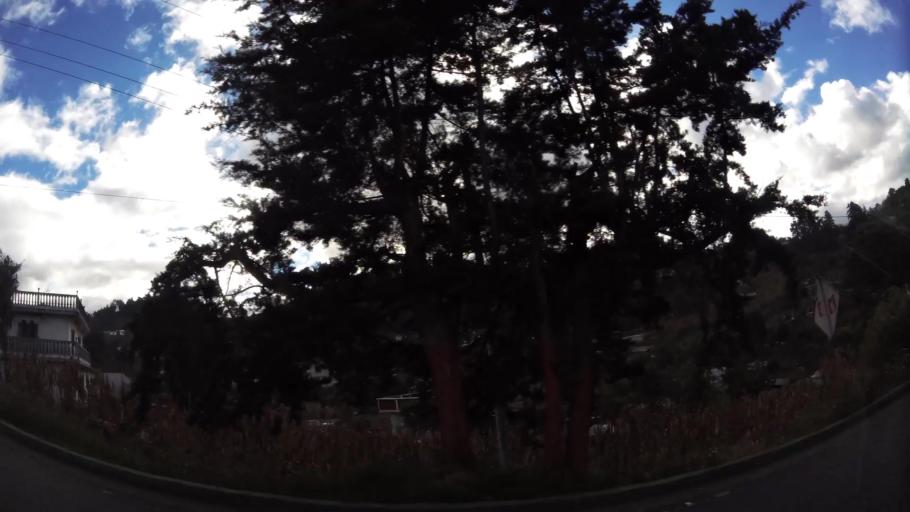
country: GT
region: Quiche
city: Chichicastenango
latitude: 14.9306
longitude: -91.1092
